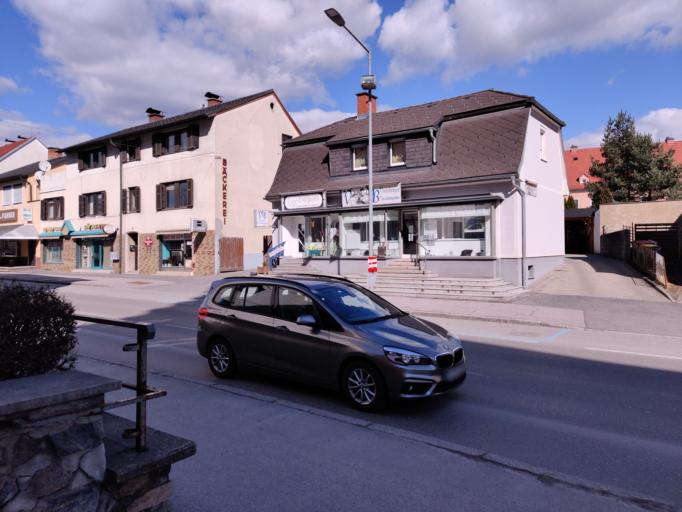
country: AT
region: Styria
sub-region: Politischer Bezirk Voitsberg
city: Voitsberg
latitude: 47.0513
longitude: 15.1437
